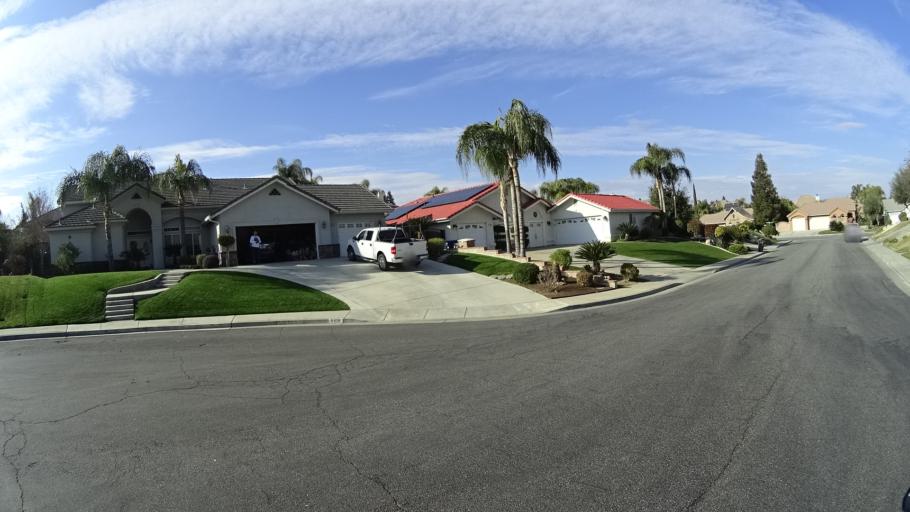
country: US
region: California
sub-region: Kern County
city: Oildale
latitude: 35.4005
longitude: -118.9159
